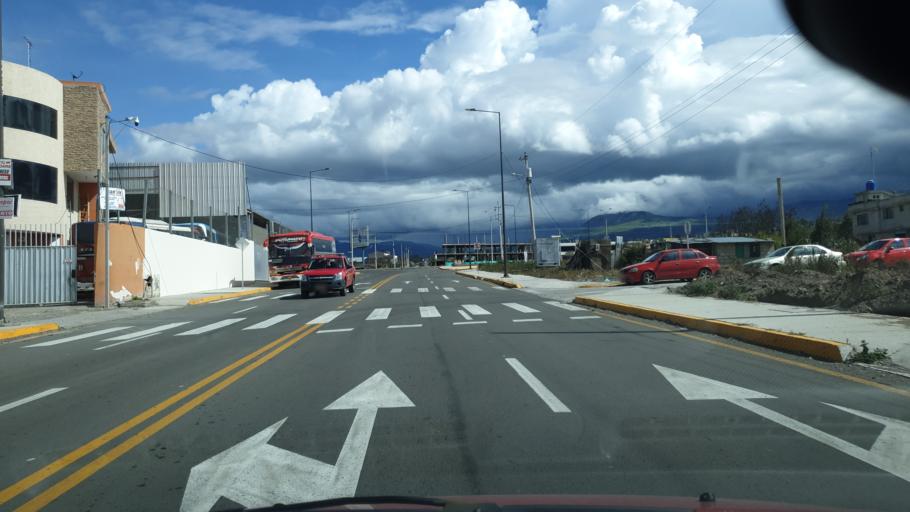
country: EC
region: Tungurahua
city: Ambato
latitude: -1.2992
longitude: -78.6319
